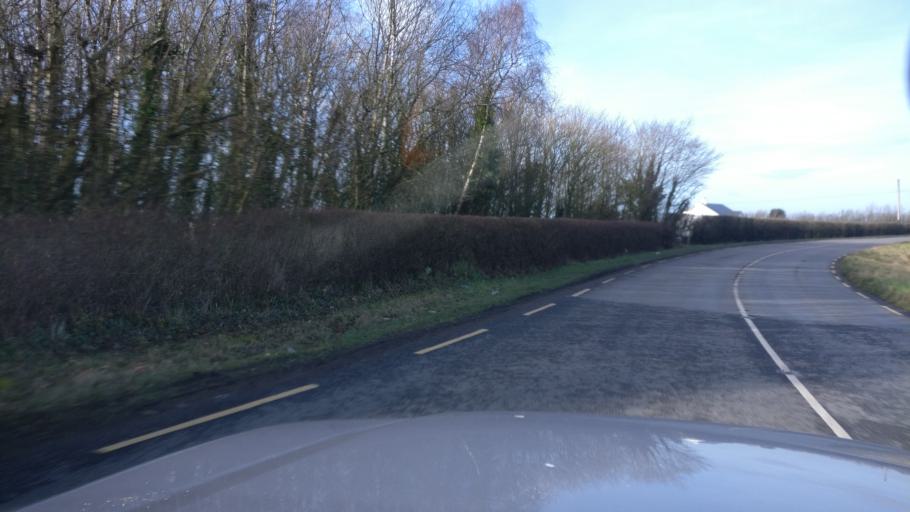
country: IE
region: Leinster
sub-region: Laois
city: Portlaoise
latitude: 53.0117
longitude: -7.2747
